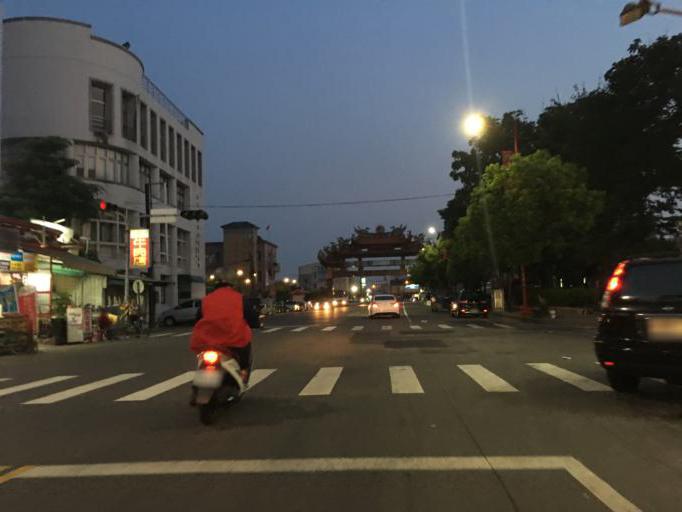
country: TW
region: Taiwan
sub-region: Chiayi
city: Taibao
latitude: 23.5528
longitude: 120.3474
